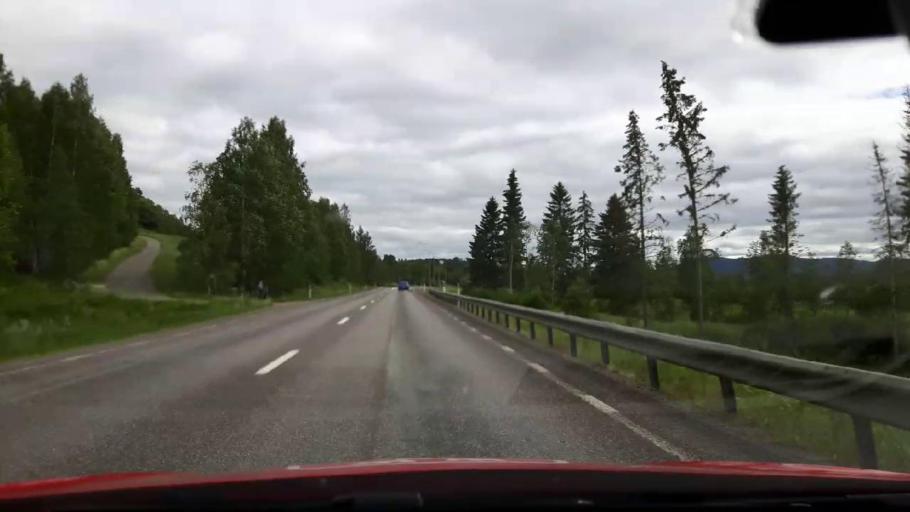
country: SE
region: Jaemtland
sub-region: Ragunda Kommun
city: Hammarstrand
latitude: 63.1204
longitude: 16.3626
